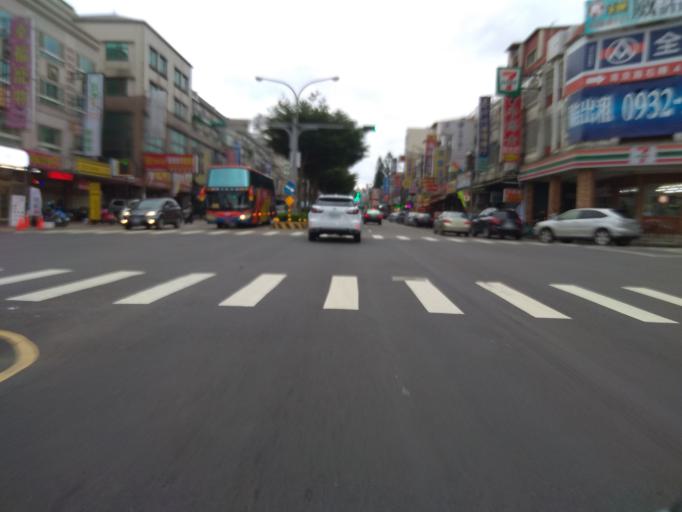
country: TW
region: Taiwan
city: Daxi
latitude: 24.9165
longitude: 121.2108
